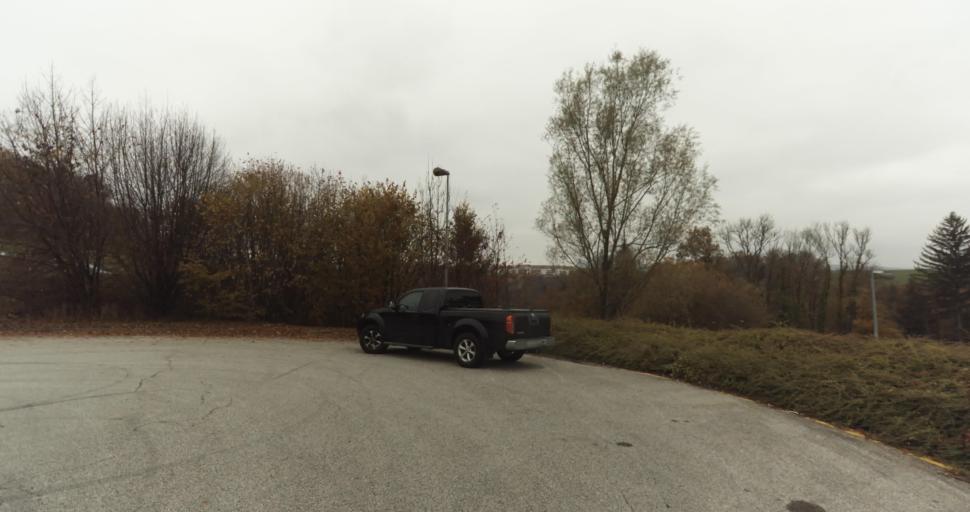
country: FR
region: Rhone-Alpes
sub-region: Departement de la Haute-Savoie
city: Seynod
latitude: 45.9000
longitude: 6.0789
